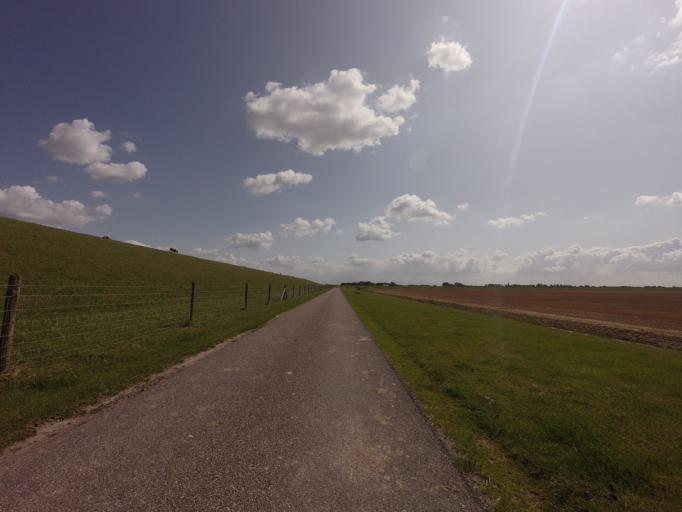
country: NL
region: Friesland
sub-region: Gemeente Ferwerderadiel
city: Hallum
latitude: 53.3205
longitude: 5.7490
